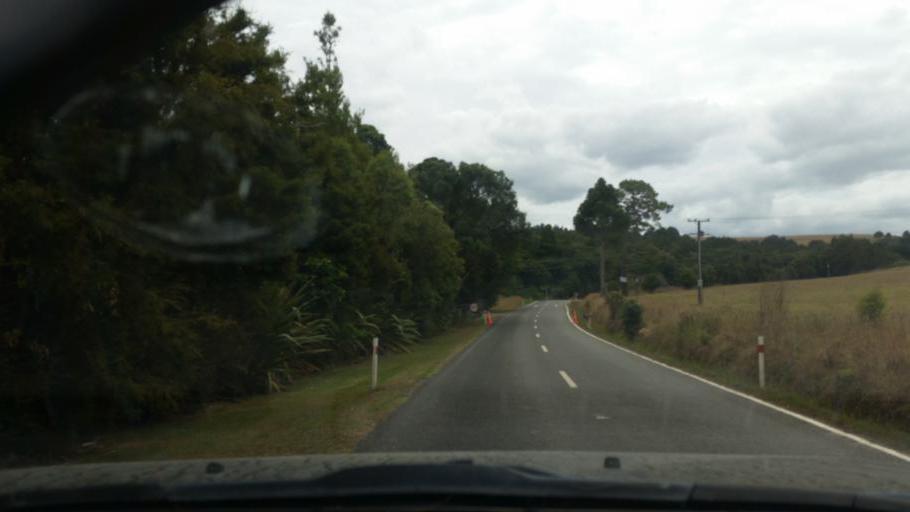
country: NZ
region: Northland
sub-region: Kaipara District
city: Dargaville
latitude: -35.7207
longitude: 173.6525
